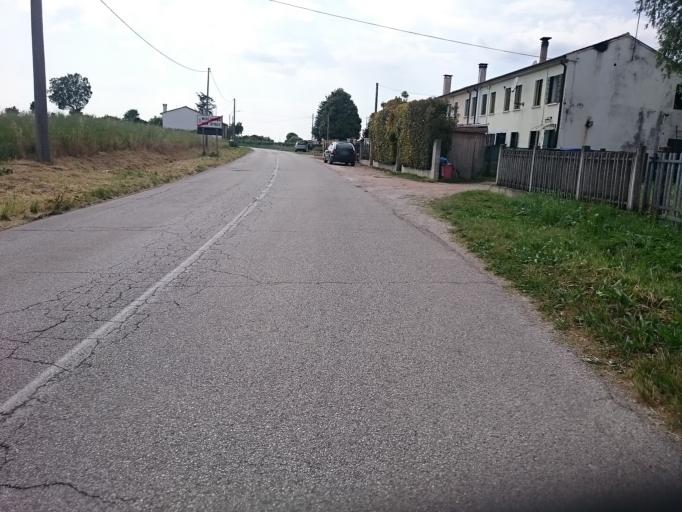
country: IT
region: Veneto
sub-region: Provincia di Padova
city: Megliadino San Vitale
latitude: 45.1959
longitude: 11.5169
